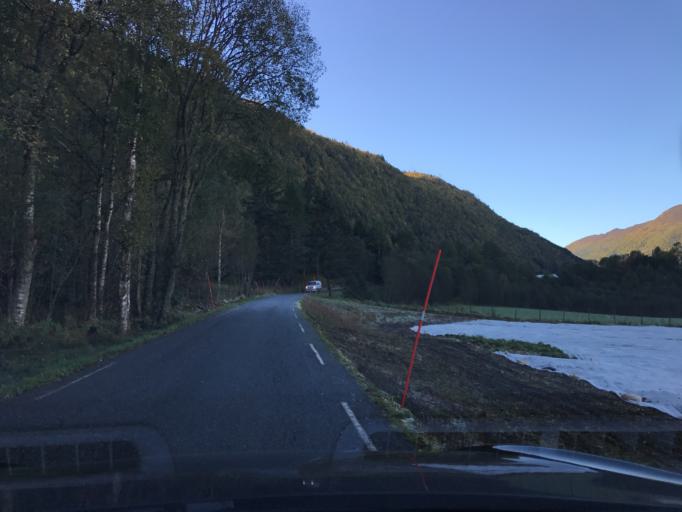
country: NO
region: More og Romsdal
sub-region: Norddal
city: Valldal
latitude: 62.3152
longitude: 7.3174
